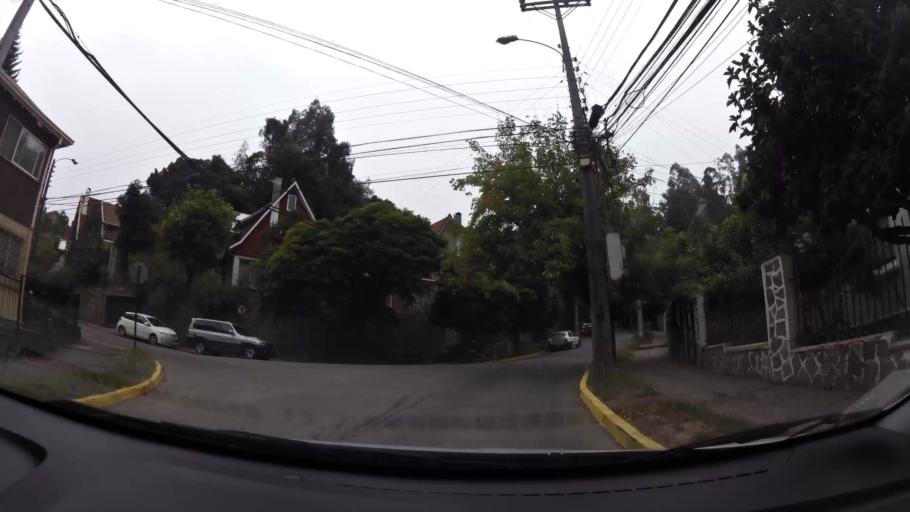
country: CL
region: Biobio
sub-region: Provincia de Concepcion
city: Concepcion
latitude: -36.8254
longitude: -73.0326
